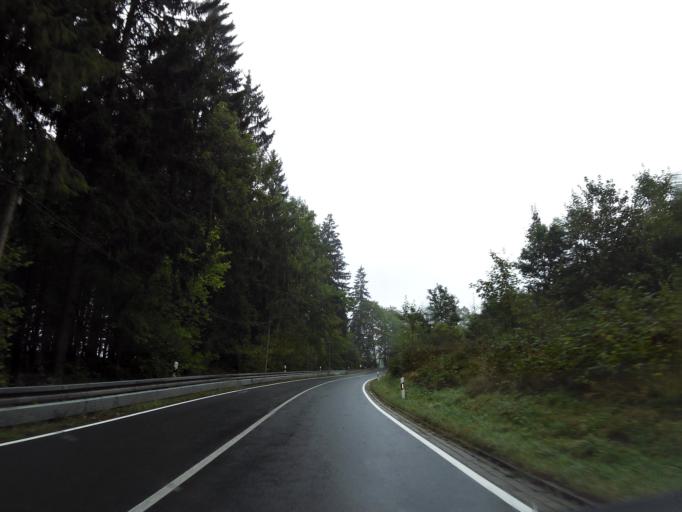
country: DE
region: Saxony-Anhalt
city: Hasselfelde
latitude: 51.6495
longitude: 10.9217
